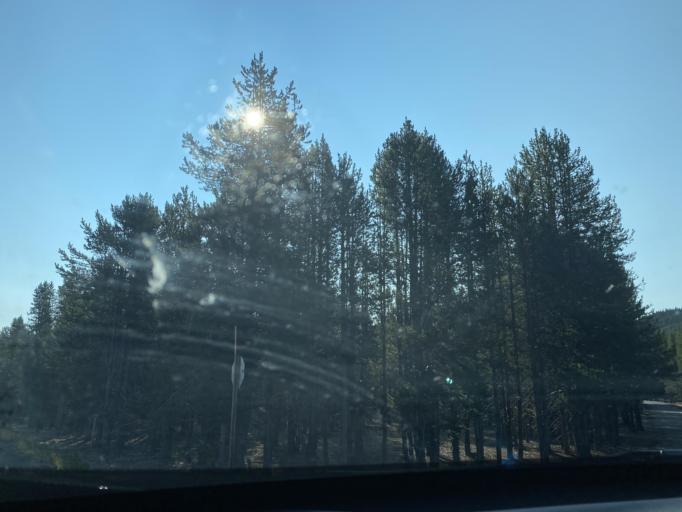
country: US
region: Oregon
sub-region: Deschutes County
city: Three Rivers
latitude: 43.7074
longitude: -121.2374
